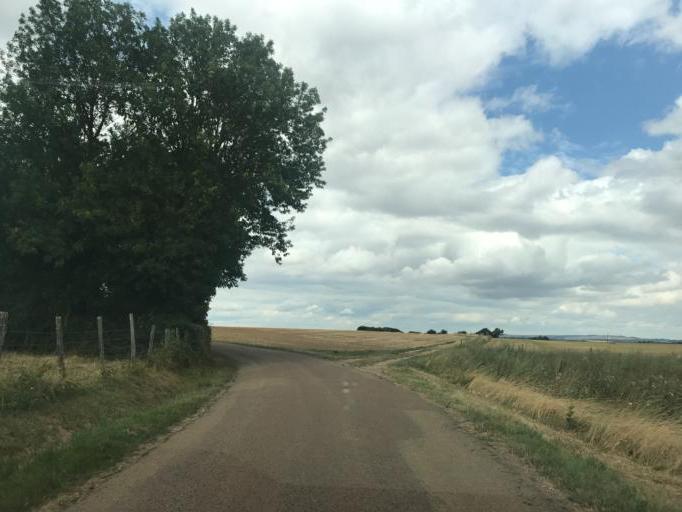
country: FR
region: Bourgogne
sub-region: Departement de l'Yonne
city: Fontenailles
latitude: 47.5065
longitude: 3.3463
